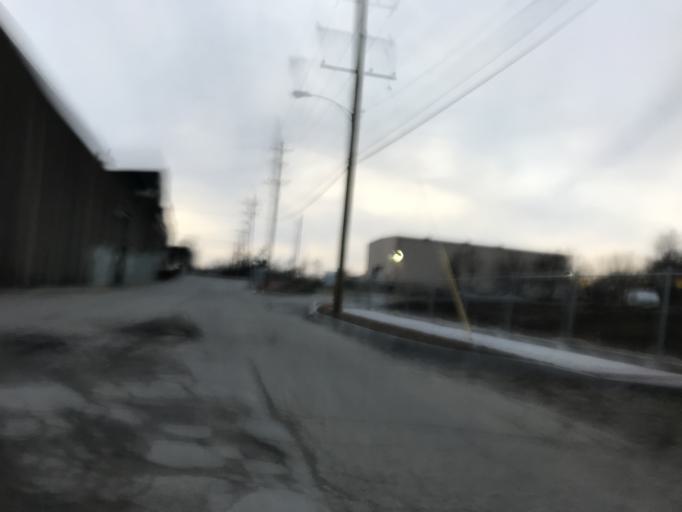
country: US
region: Indiana
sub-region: Clark County
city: Jeffersonville
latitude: 38.2577
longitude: -85.7297
